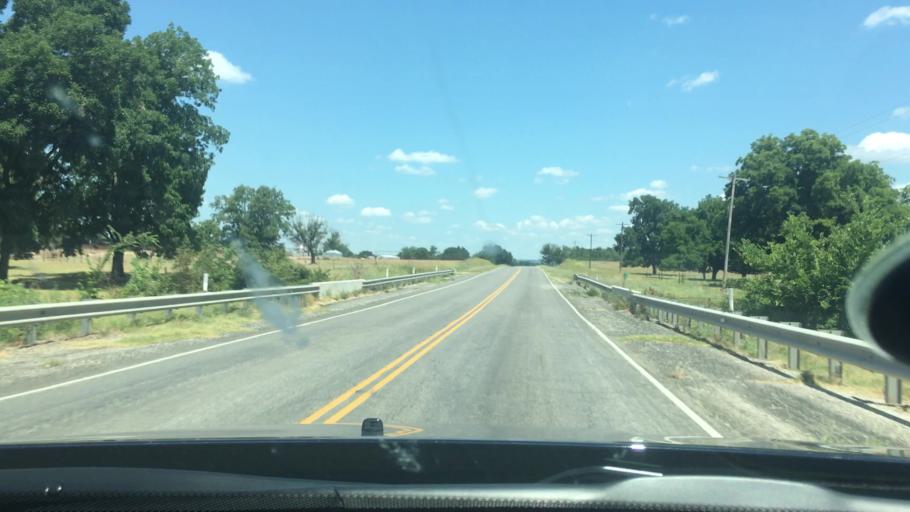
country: US
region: Oklahoma
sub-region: Carter County
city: Dickson
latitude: 34.2114
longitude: -96.9771
